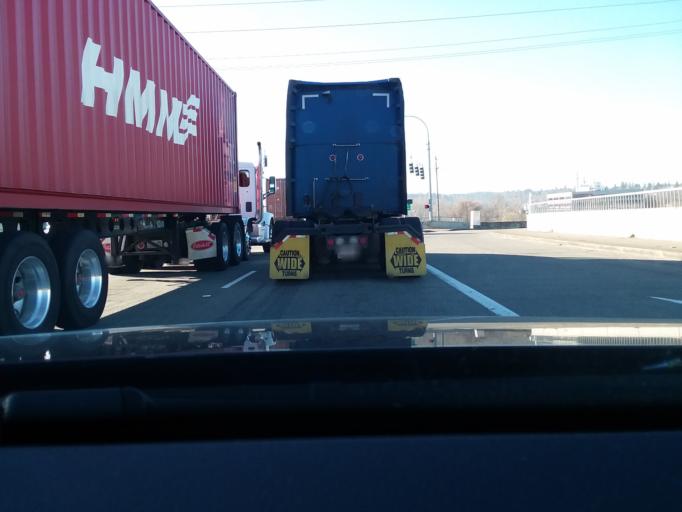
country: US
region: Washington
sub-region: Pierce County
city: Fife
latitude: 47.2482
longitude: -122.3857
